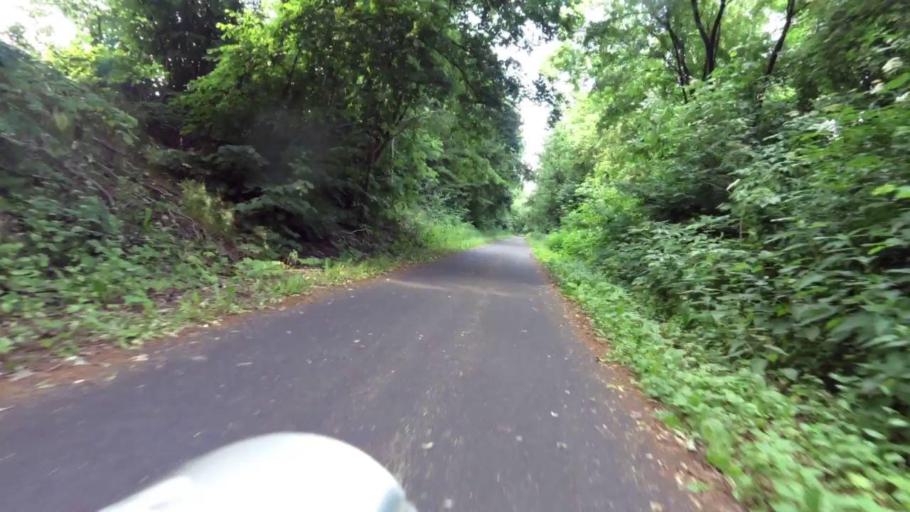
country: PL
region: Kujawsko-Pomorskie
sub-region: Powiat torunski
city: Lubianka
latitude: 53.0866
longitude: 18.5353
